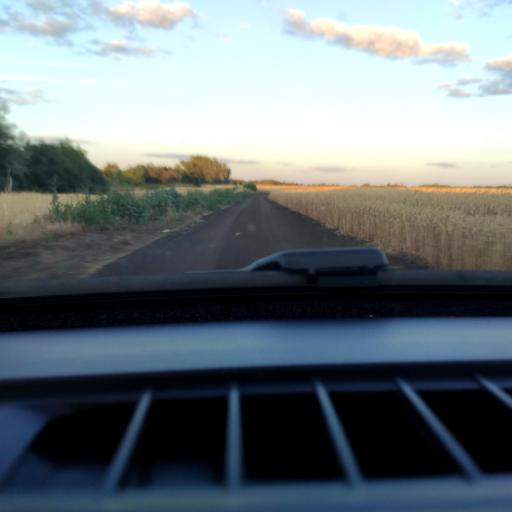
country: RU
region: Voronezj
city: Verkhnyaya Khava
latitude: 51.5906
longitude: 39.8609
